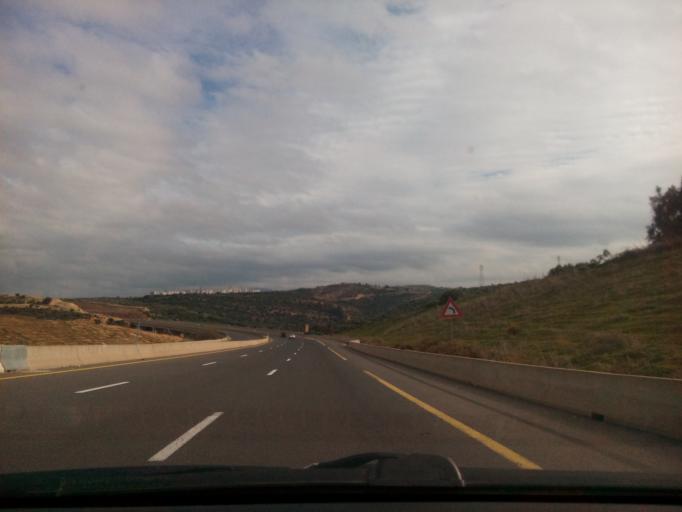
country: DZ
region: Tlemcen
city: Chetouane
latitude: 34.9413
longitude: -1.3185
